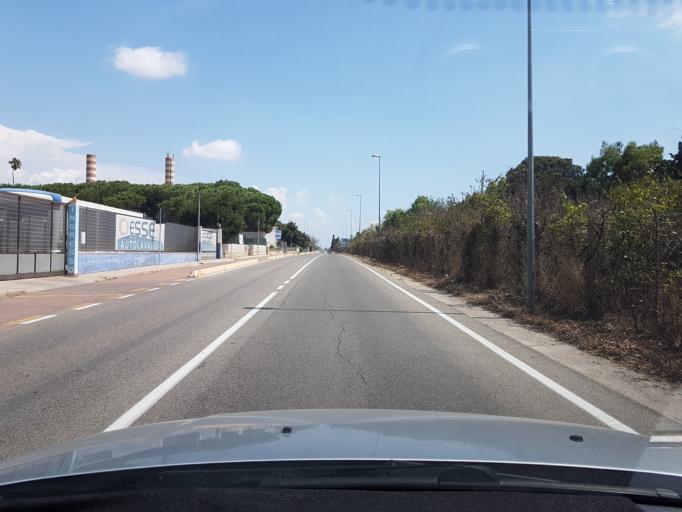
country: IT
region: Sardinia
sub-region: Provincia di Oristano
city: Oristano
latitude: 39.9103
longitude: 8.6047
